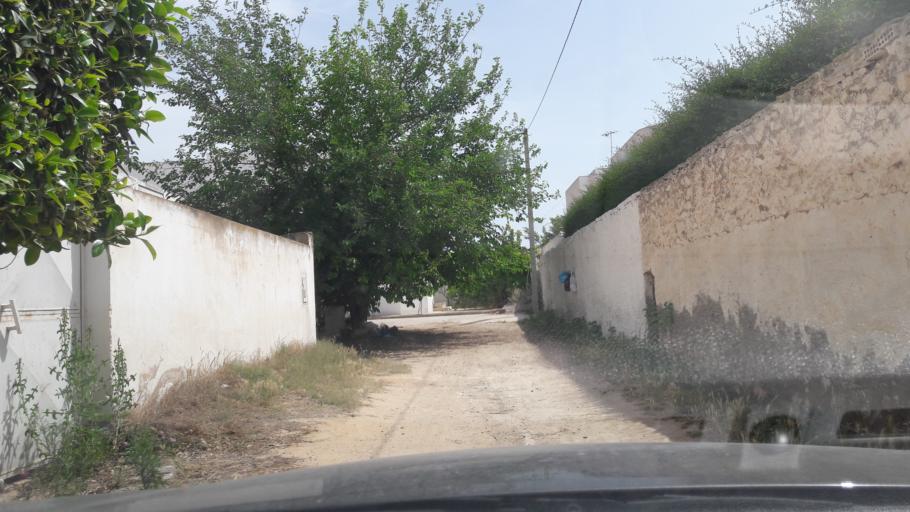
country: TN
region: Safaqis
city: Al Qarmadah
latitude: 34.7862
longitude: 10.7582
